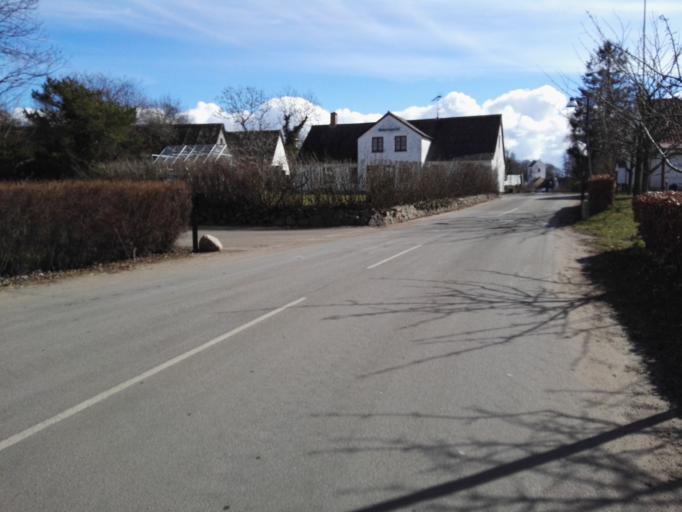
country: DK
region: Zealand
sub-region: Lejre Kommune
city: Ejby
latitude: 55.7681
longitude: 11.8033
